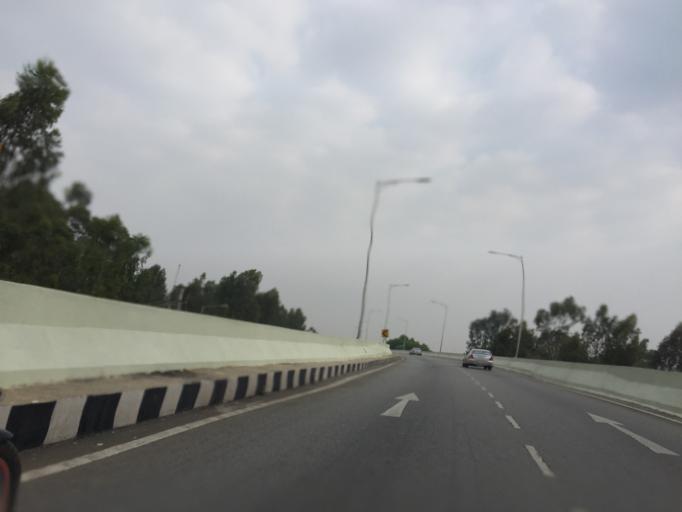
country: IN
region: Karnataka
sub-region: Bangalore Rural
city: Devanhalli
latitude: 13.1996
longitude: 77.6578
